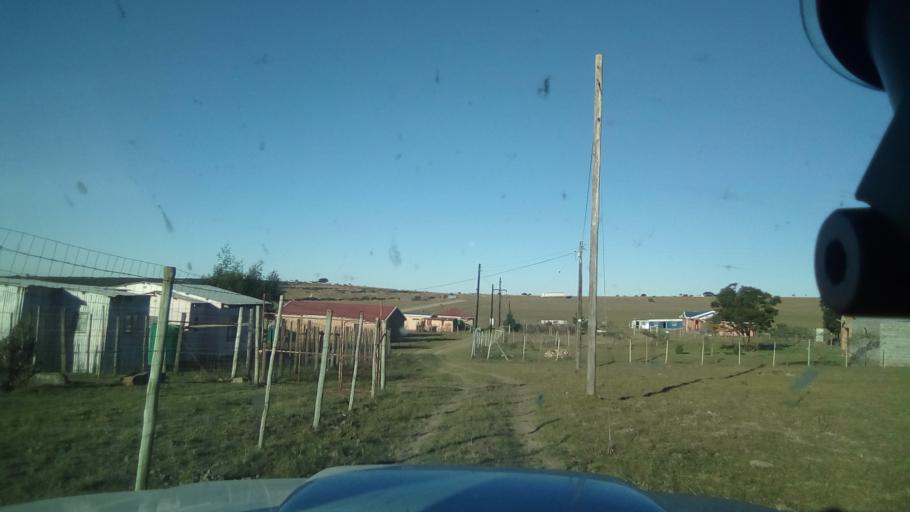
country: ZA
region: Eastern Cape
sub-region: Buffalo City Metropolitan Municipality
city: Bhisho
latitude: -32.9528
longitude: 27.2949
